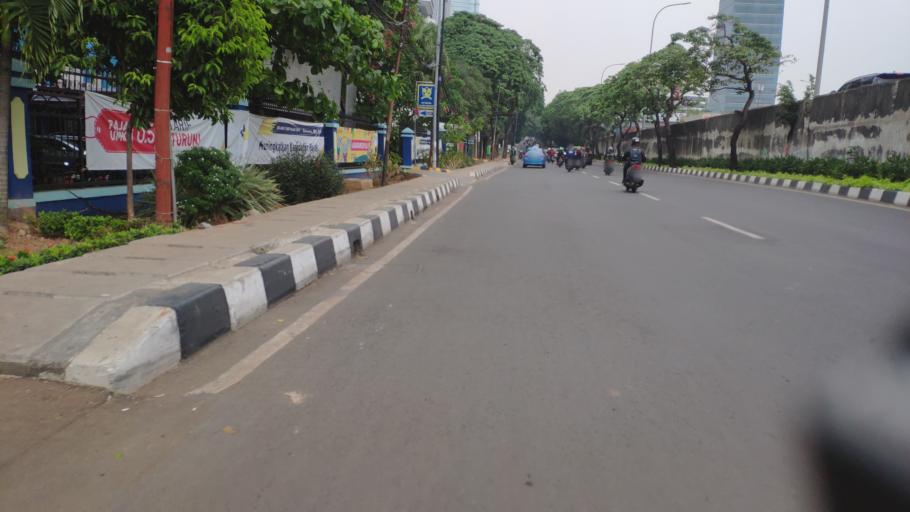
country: ID
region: Jakarta Raya
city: Jakarta
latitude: -6.3009
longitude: 106.8347
